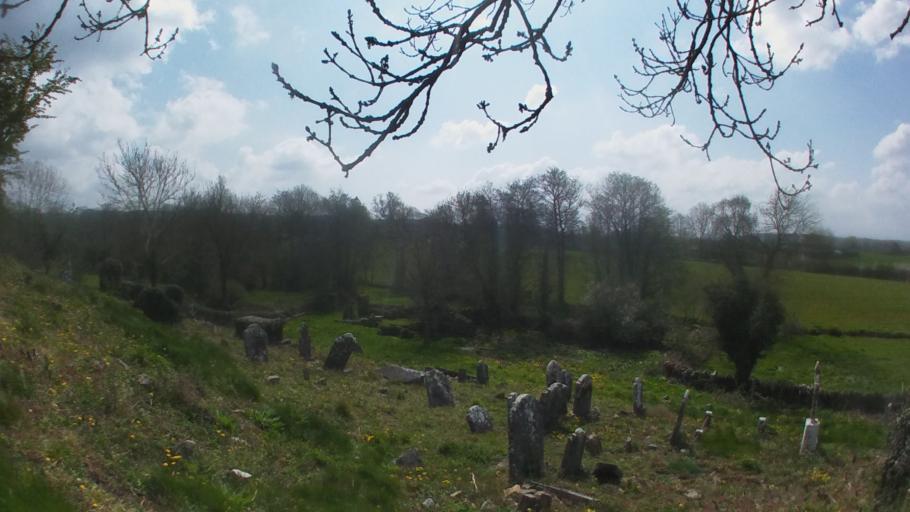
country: IE
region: Leinster
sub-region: Kilkenny
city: Thomastown
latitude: 52.5315
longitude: -7.1238
